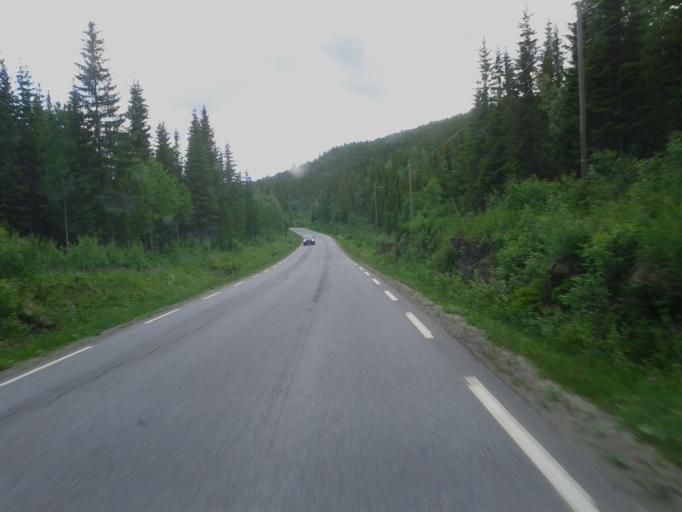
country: NO
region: Nordland
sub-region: Grane
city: Trofors
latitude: 65.5337
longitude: 13.6744
